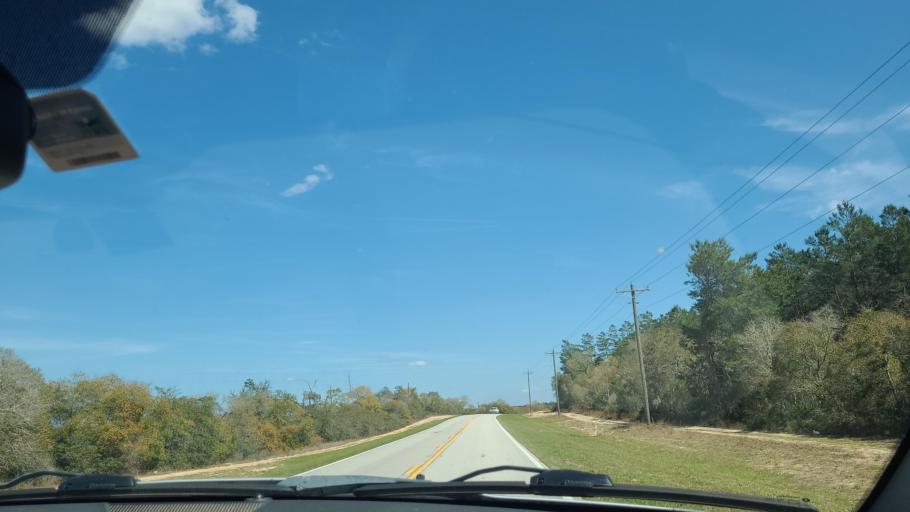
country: US
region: Florida
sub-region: Putnam County
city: Interlachen
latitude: 29.3691
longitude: -81.8408
